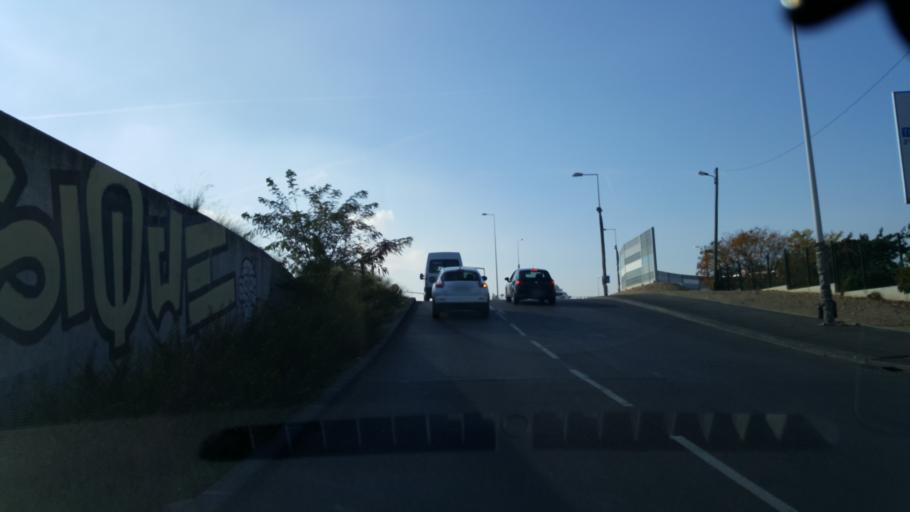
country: FR
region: Provence-Alpes-Cote d'Azur
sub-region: Departement des Bouches-du-Rhone
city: Marseille 11
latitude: 43.2859
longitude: 5.4271
